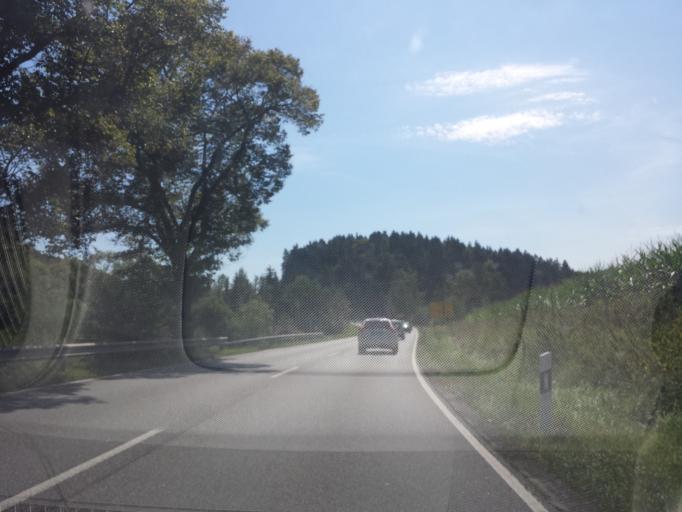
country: DE
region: Bavaria
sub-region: Upper Palatinate
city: Traitsching
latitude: 49.1410
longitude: 12.6507
